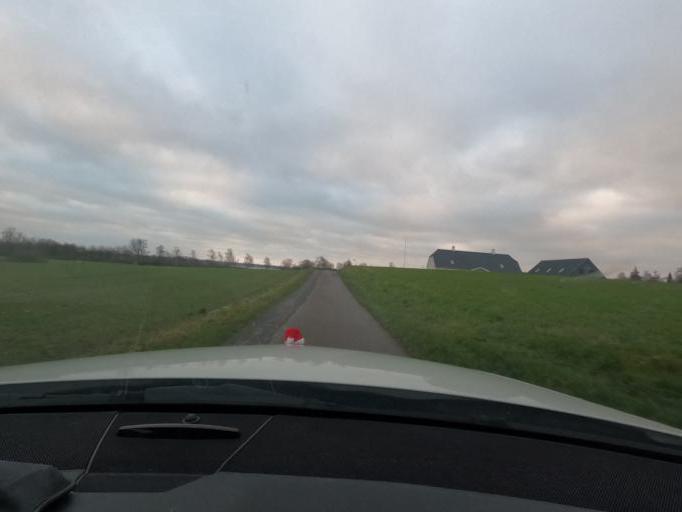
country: DK
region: South Denmark
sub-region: Sonderborg Kommune
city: Sonderborg
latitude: 54.9009
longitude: 9.8522
